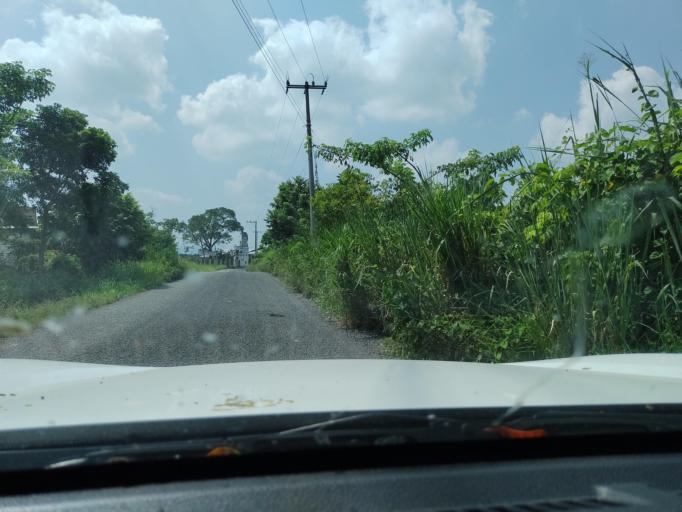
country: MX
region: Veracruz
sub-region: Atzalan
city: Colonias Pedernales
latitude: 20.0633
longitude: -97.0257
